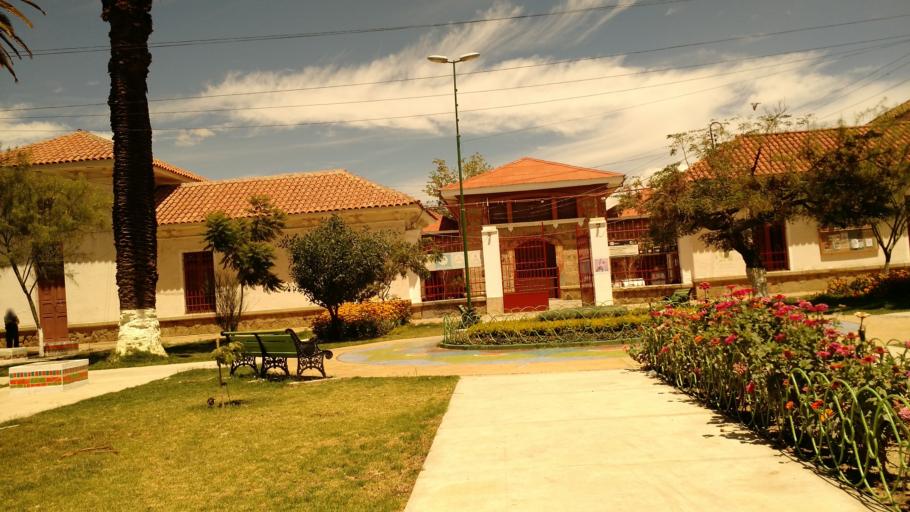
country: BO
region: Cochabamba
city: Cochabamba
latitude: -17.4002
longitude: -66.1651
